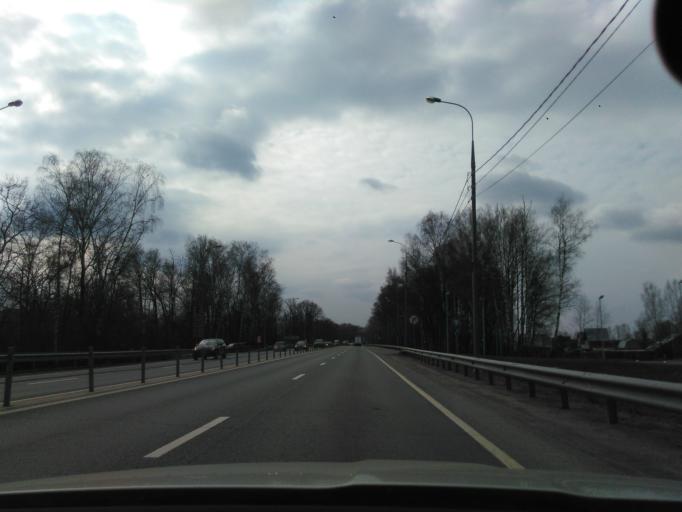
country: RU
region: Moskovskaya
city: Marfino
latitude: 56.0191
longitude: 37.5451
